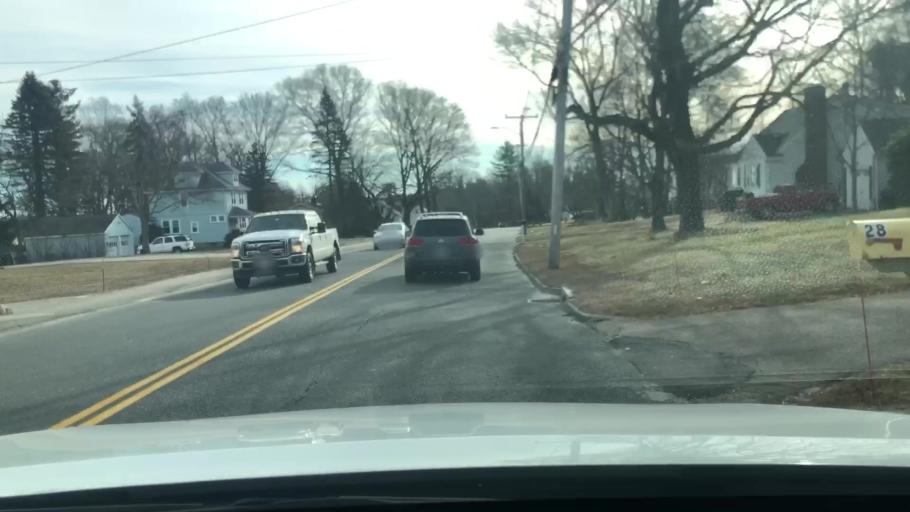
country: US
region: Massachusetts
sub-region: Worcester County
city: Hopedale
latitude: 42.1437
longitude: -71.5369
